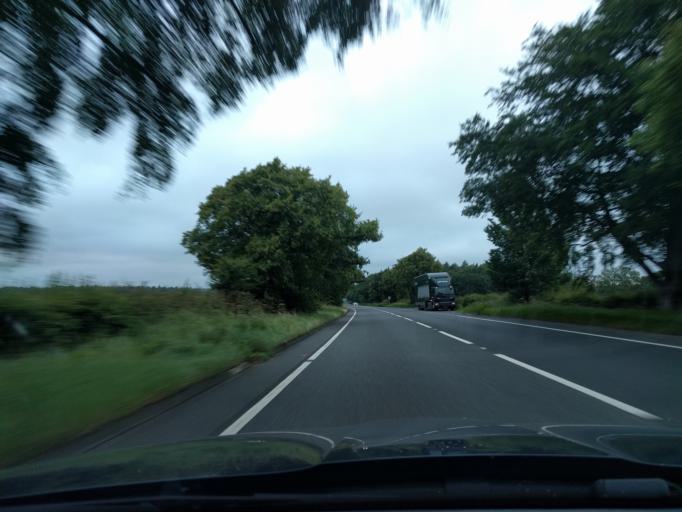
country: GB
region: England
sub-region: Northumberland
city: Hebron
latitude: 55.2103
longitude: -1.7102
